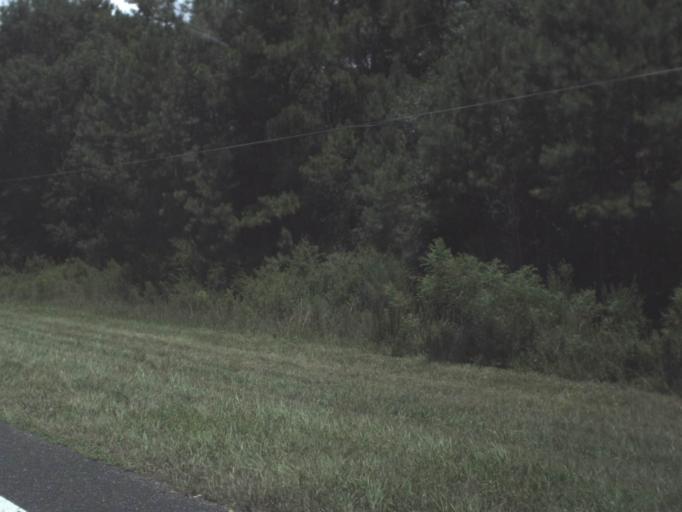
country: US
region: Florida
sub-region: Taylor County
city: Perry
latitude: 30.0475
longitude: -83.5504
